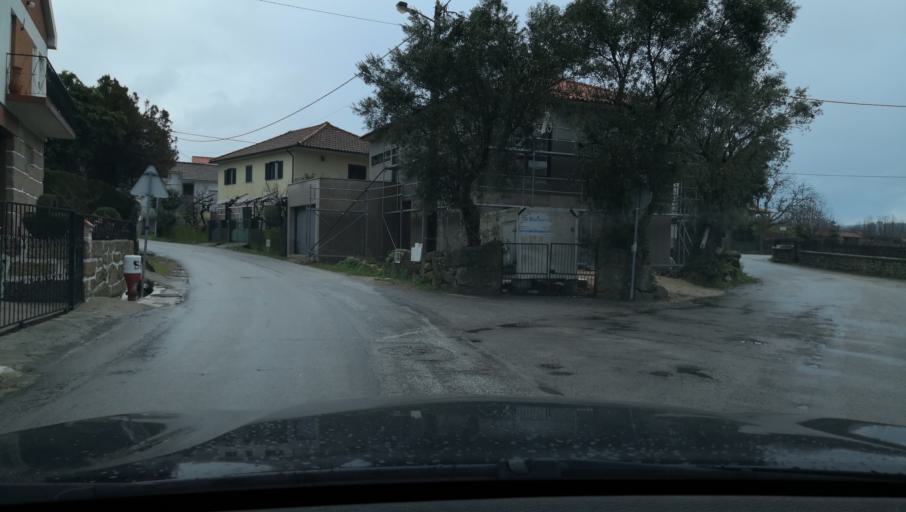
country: PT
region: Vila Real
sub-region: Vila Real
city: Vila Real
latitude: 41.3315
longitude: -7.7253
